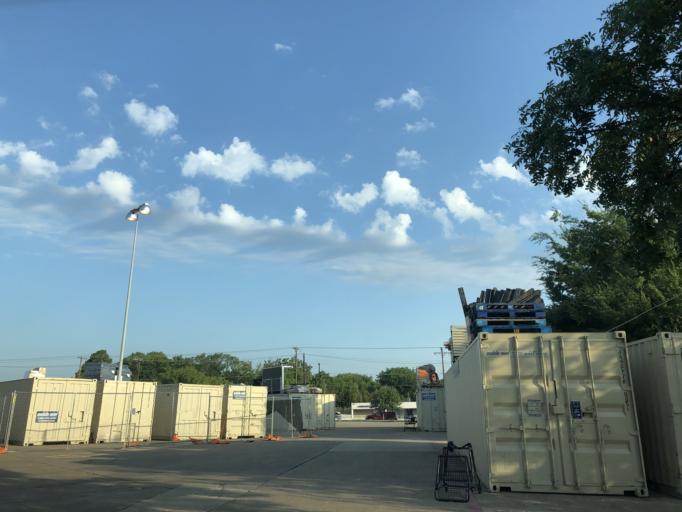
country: US
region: Texas
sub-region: Dallas County
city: Sunnyvale
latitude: 32.8465
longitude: -96.5935
